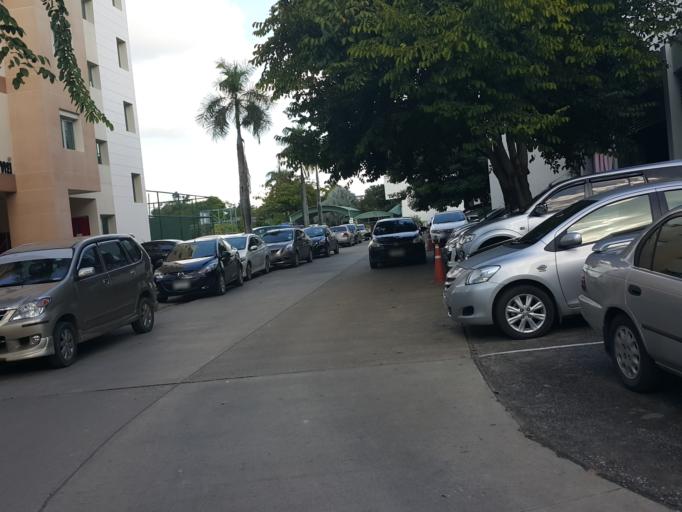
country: TH
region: Lampang
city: Lampang
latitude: 18.2879
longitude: 99.5054
